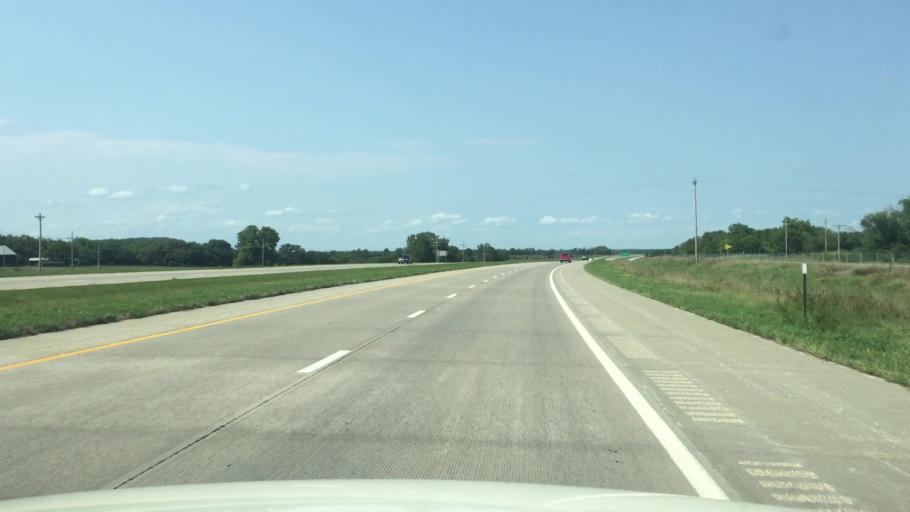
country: US
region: Kansas
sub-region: Linn County
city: Pleasanton
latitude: 38.1942
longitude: -94.7052
